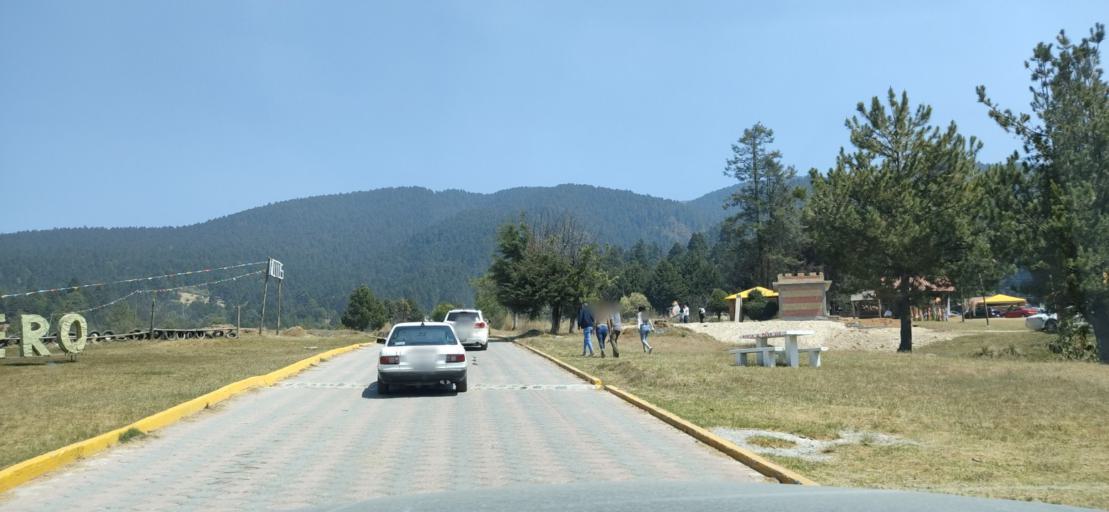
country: MX
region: Mexico
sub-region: Ocoyoacac
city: San Jeronimo Acazulco
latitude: 19.2421
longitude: -99.3795
